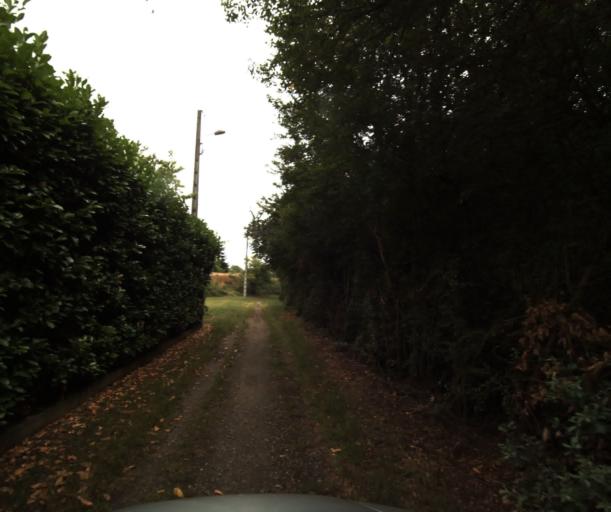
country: FR
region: Midi-Pyrenees
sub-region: Departement de la Haute-Garonne
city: Pinsaguel
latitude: 43.5075
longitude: 1.3879
